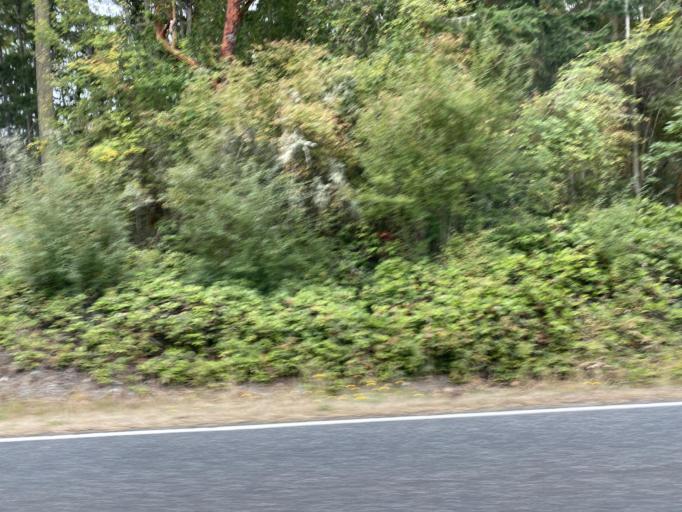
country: US
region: Washington
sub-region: Island County
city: Coupeville
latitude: 48.2251
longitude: -122.7318
